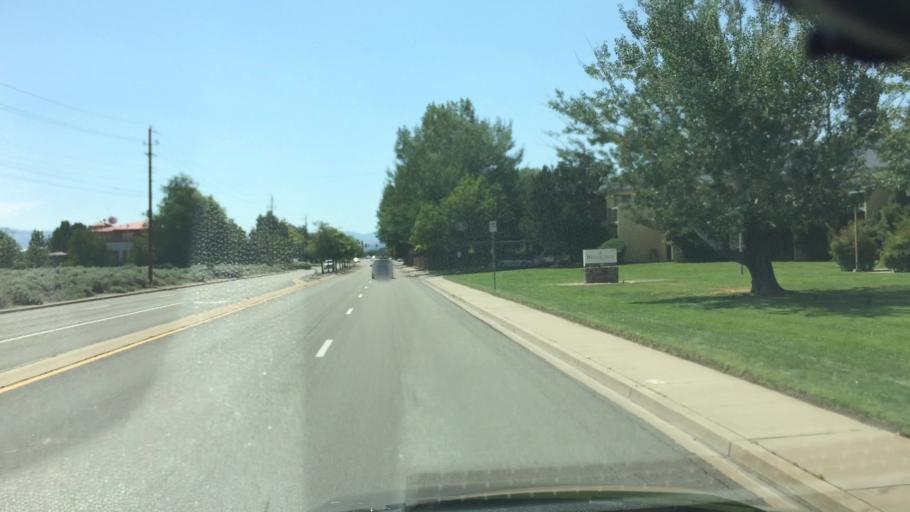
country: US
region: Nevada
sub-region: Washoe County
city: Sparks
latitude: 39.5420
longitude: -119.7075
